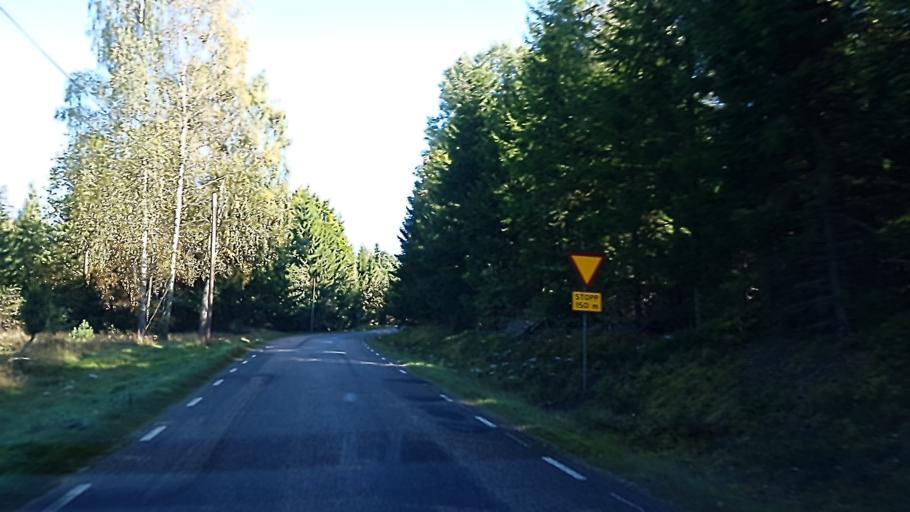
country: SE
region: Kronoberg
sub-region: Ljungby Kommun
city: Ljungby
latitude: 56.8243
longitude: 14.0520
